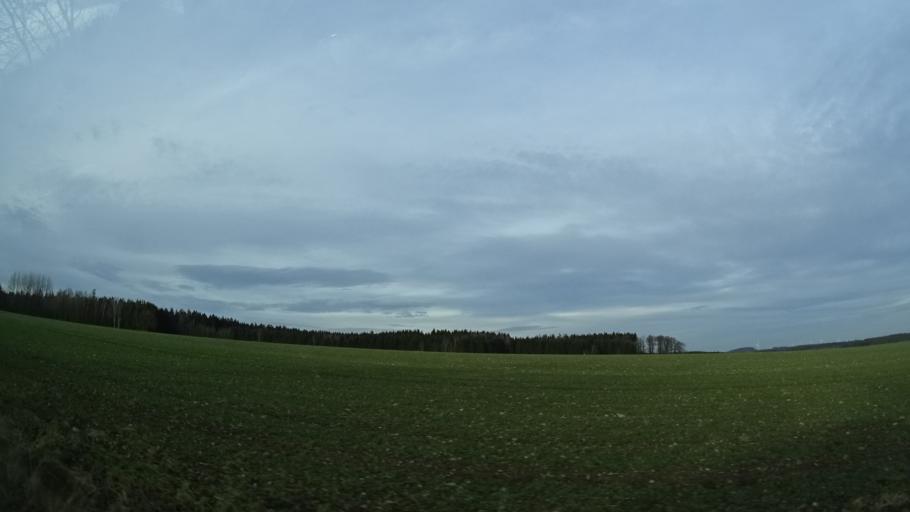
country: DE
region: Thuringia
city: Chursdorf
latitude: 50.6668
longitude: 11.8394
